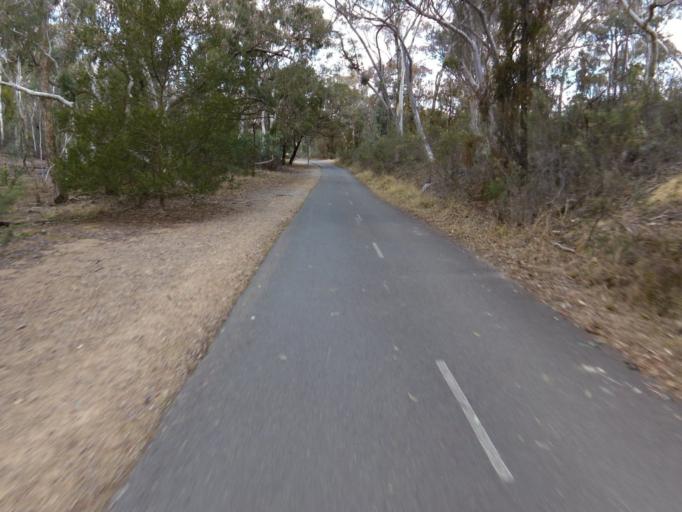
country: AU
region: Australian Capital Territory
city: Acton
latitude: -35.2540
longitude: 149.1087
